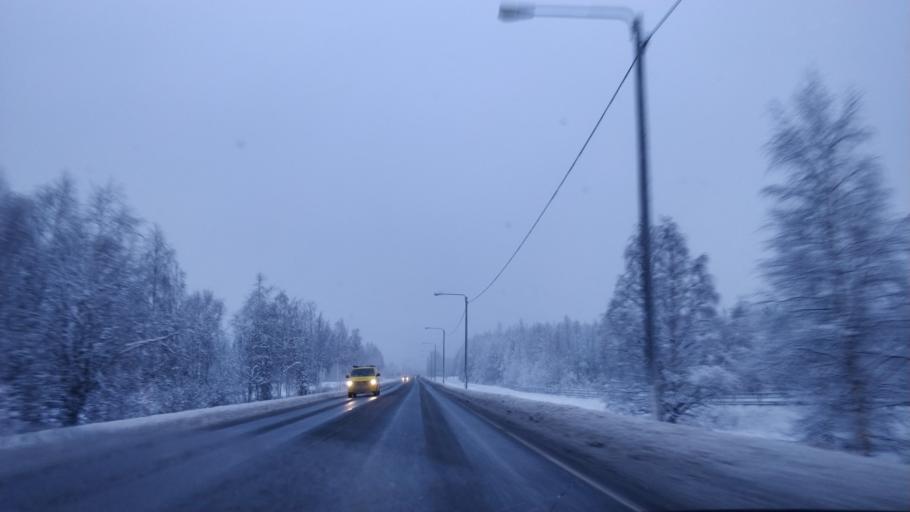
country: FI
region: Lapland
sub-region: Rovaniemi
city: Rovaniemi
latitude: 66.4731
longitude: 25.6180
